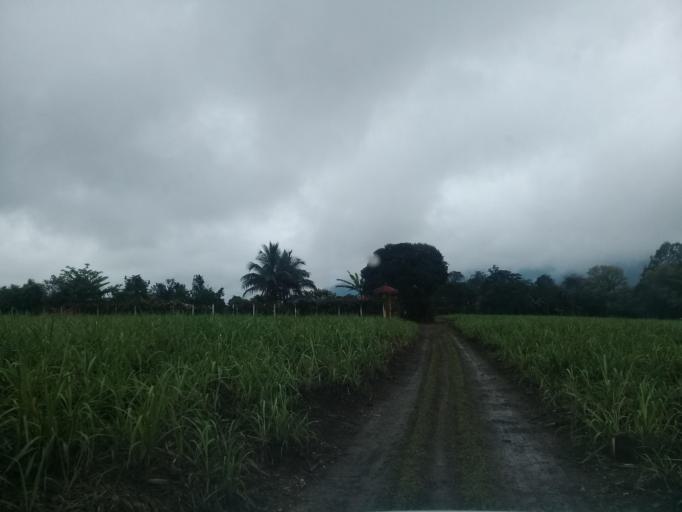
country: MX
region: Veracruz
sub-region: Amatlan de los Reyes
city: Centro de Readaptacion Social
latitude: 18.8214
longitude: -96.9543
